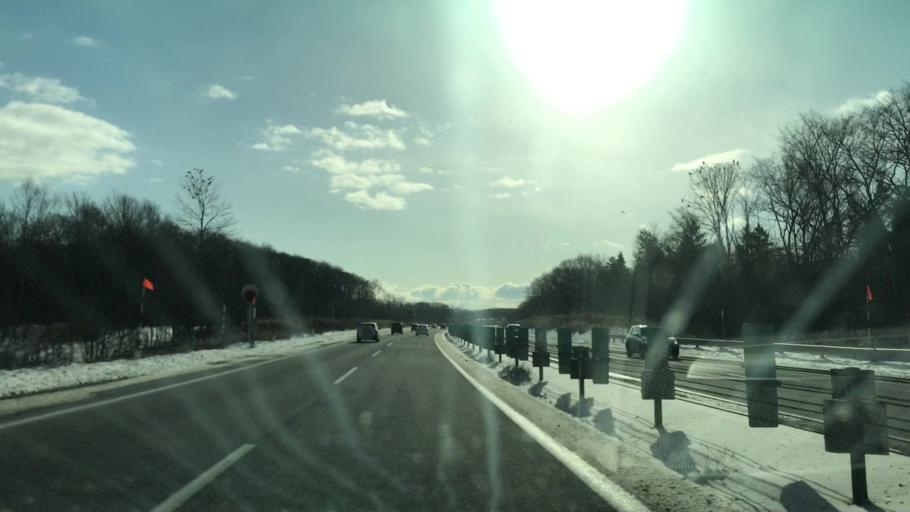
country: JP
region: Hokkaido
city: Chitose
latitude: 42.8333
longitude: 141.6096
